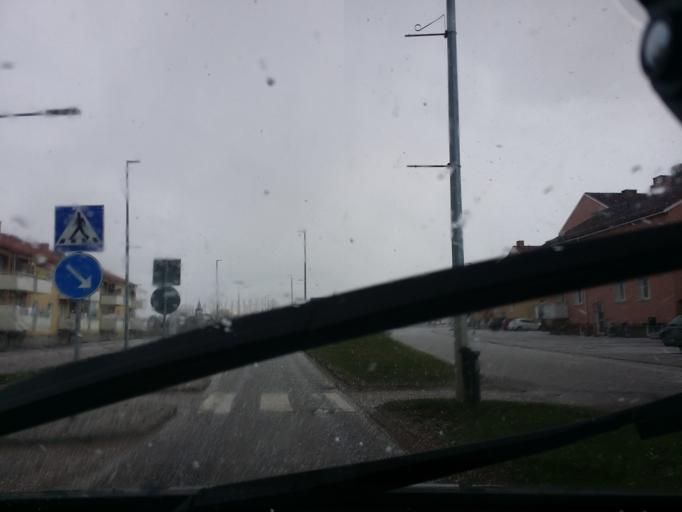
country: SE
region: Vaestmanland
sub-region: Sala Kommun
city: Sala
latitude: 59.9169
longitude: 16.6120
